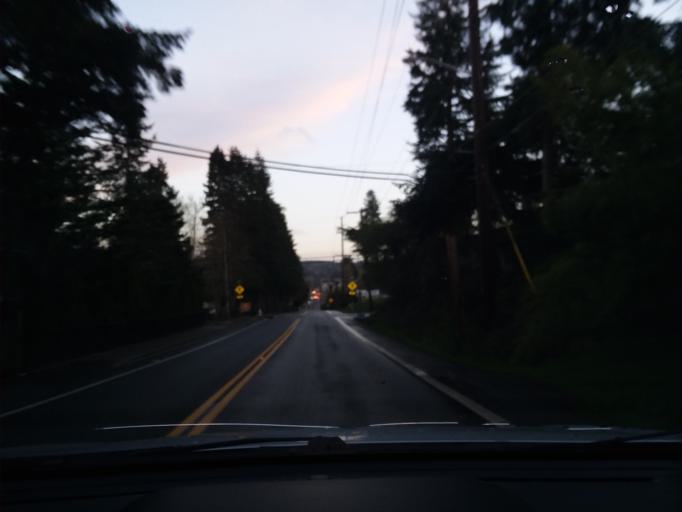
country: US
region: Washington
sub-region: King County
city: Kenmore
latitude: 47.7667
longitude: -122.2495
